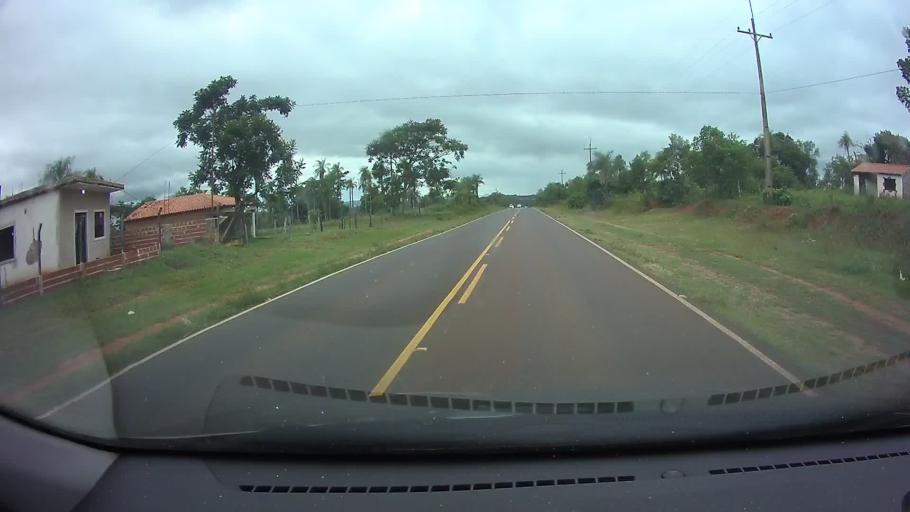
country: PY
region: Paraguari
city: Carapegua
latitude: -25.7271
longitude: -57.3153
